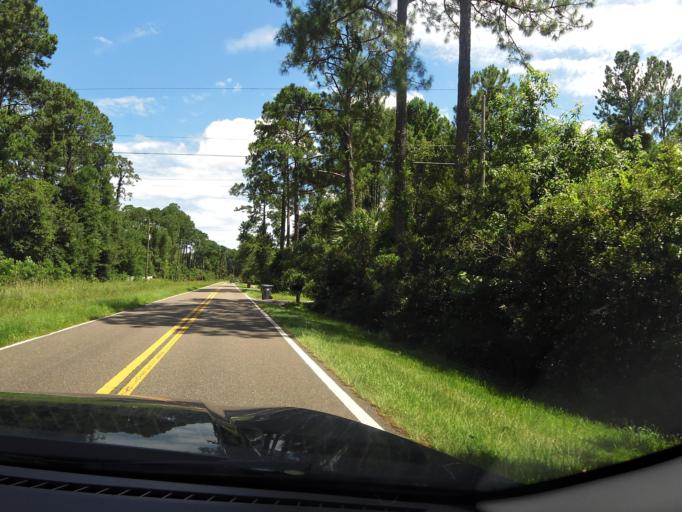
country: US
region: Georgia
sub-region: Camden County
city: St. Marys
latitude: 30.6780
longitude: -81.5326
